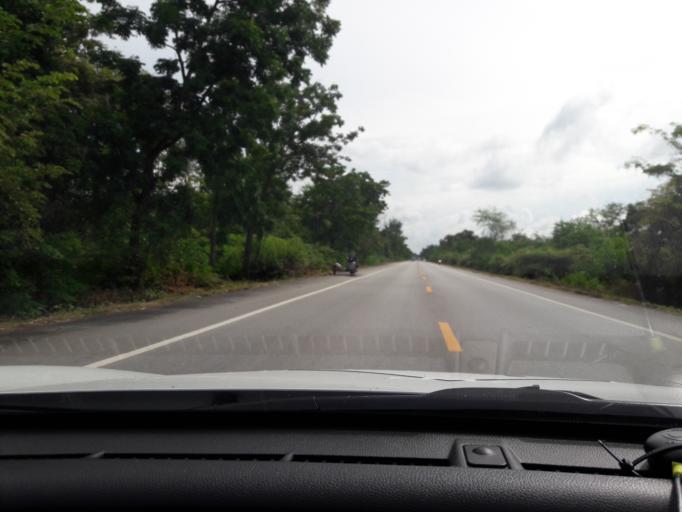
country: TH
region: Nakhon Sawan
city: Tak Fa
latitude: 15.4870
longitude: 100.5371
